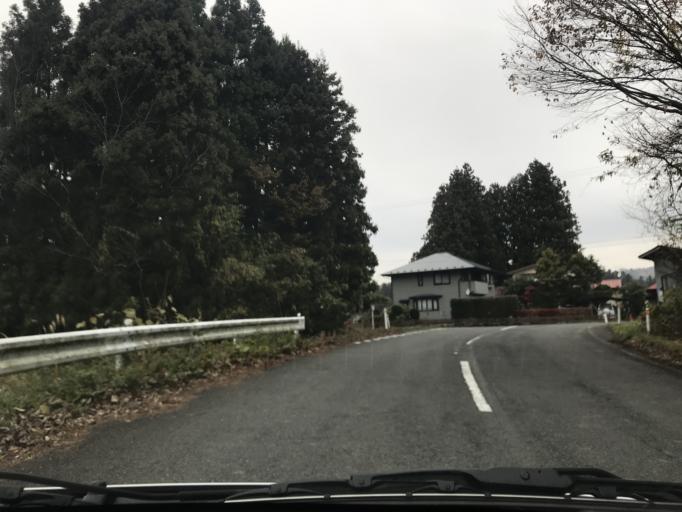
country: JP
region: Iwate
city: Mizusawa
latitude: 39.0301
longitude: 141.0721
